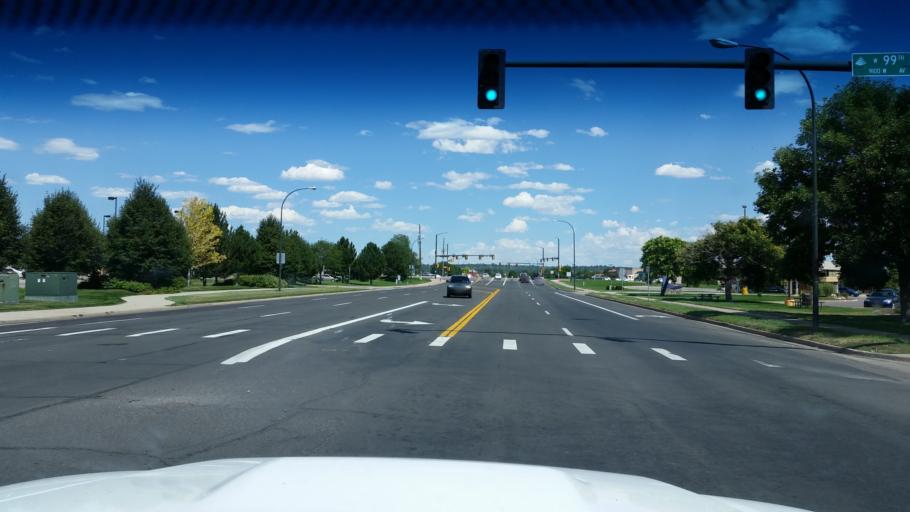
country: US
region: Colorado
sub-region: Broomfield County
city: Broomfield
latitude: 39.8781
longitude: -105.0986
